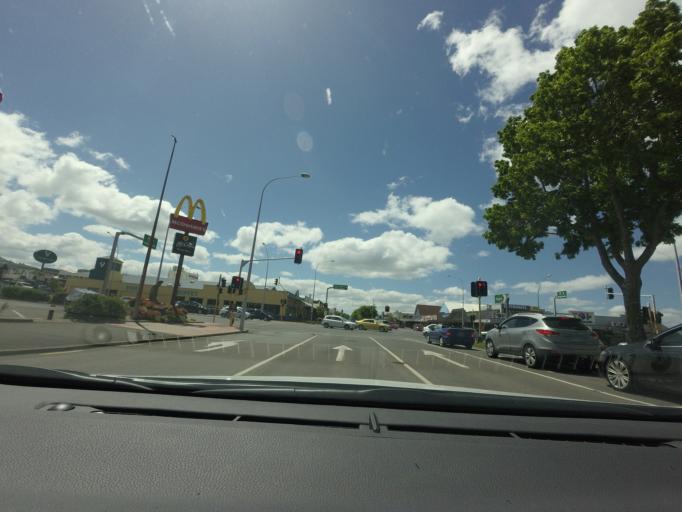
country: NZ
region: Bay of Plenty
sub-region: Rotorua District
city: Rotorua
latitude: -38.1402
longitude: 176.2537
